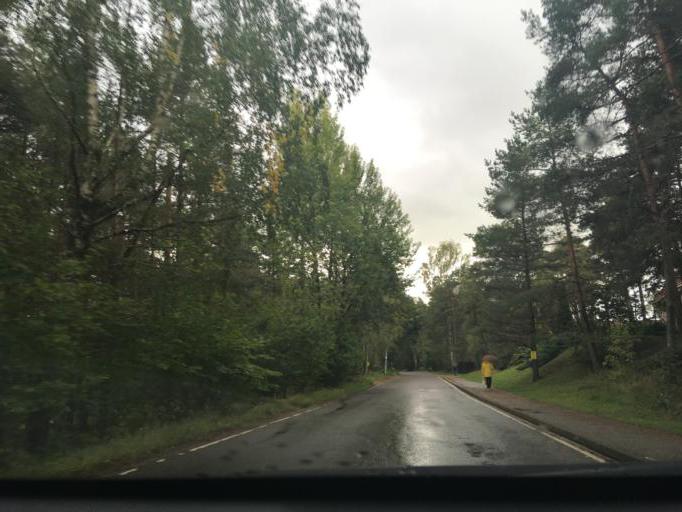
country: EE
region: Harju
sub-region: Saue vald
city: Laagri
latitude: 59.3647
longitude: 24.6446
